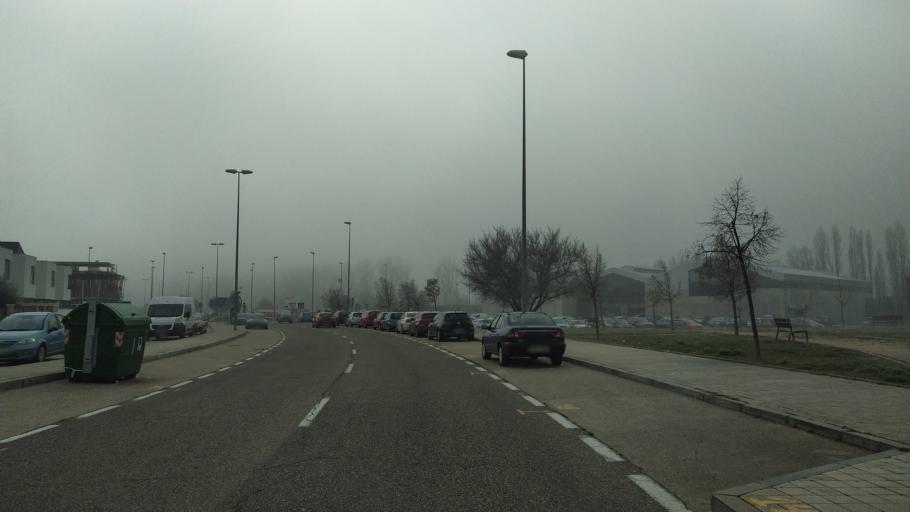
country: ES
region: Castille and Leon
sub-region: Provincia de Palencia
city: Palencia
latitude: 41.9982
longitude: -4.5329
